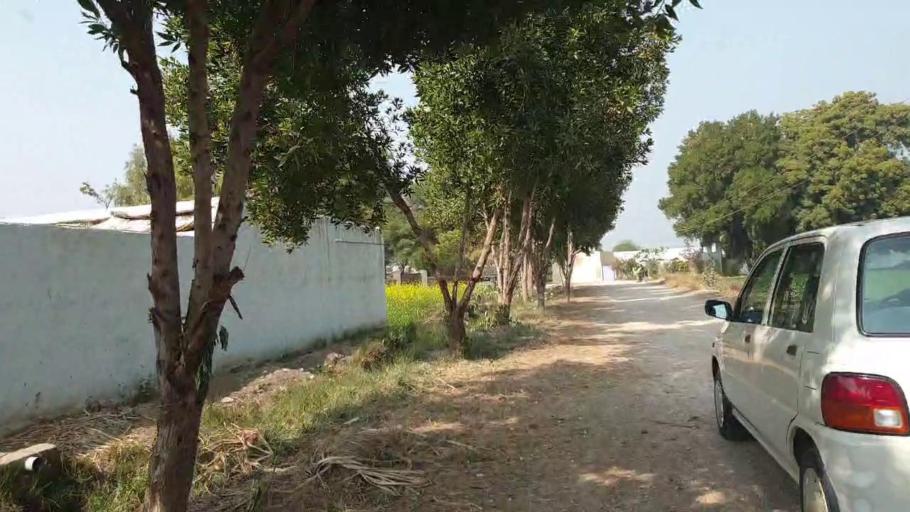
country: PK
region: Sindh
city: Hala
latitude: 25.8269
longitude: 68.4318
